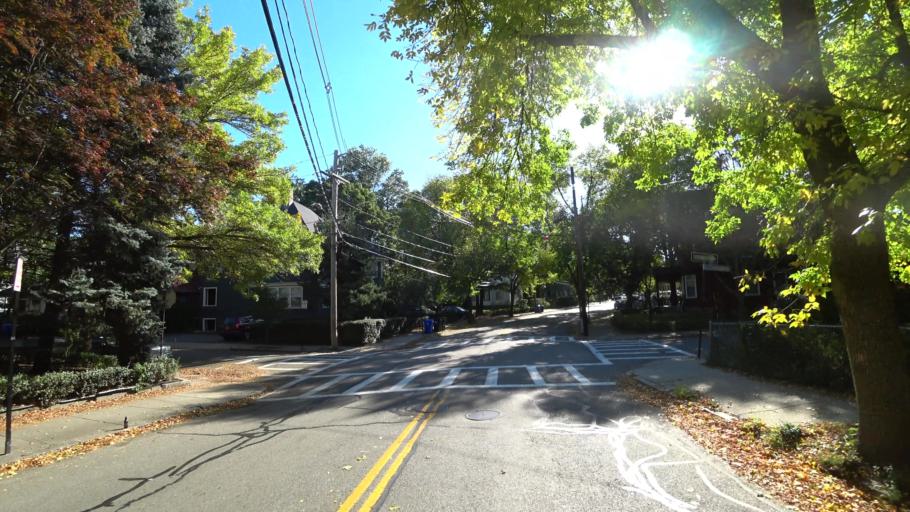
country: US
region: Massachusetts
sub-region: Norfolk County
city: Brookline
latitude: 42.3370
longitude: -71.1163
